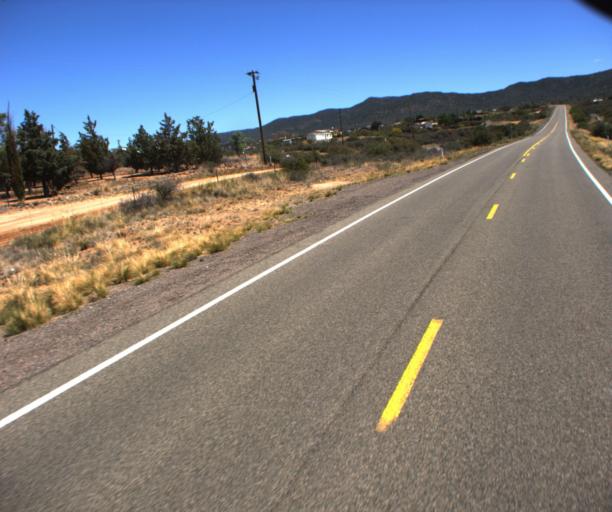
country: US
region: Arizona
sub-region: Yavapai County
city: Prescott
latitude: 34.4162
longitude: -112.6011
